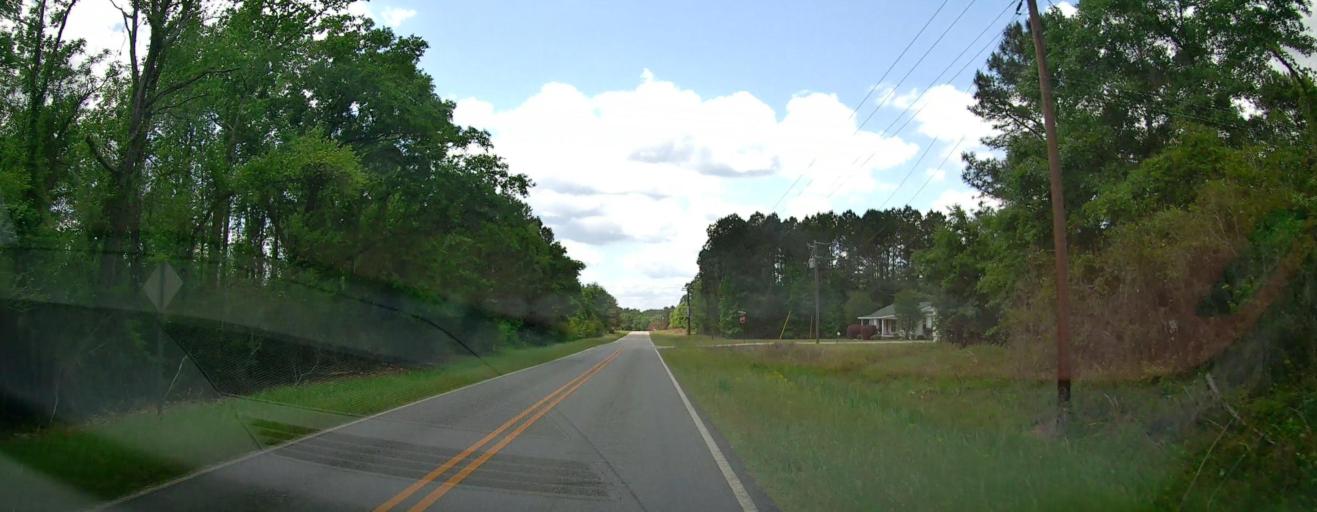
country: US
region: Georgia
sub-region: Laurens County
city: East Dublin
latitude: 32.5816
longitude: -82.7866
